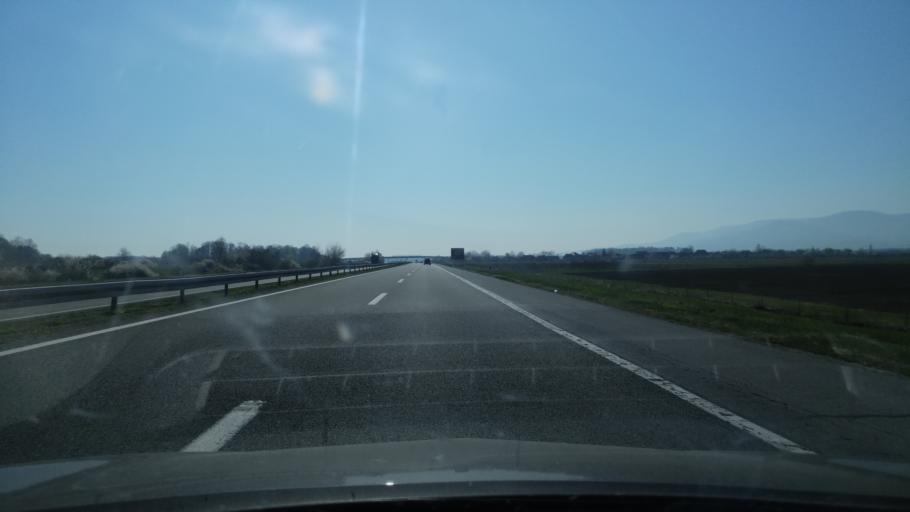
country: HR
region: Brodsko-Posavska
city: Batrina
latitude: 45.1833
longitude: 17.6418
